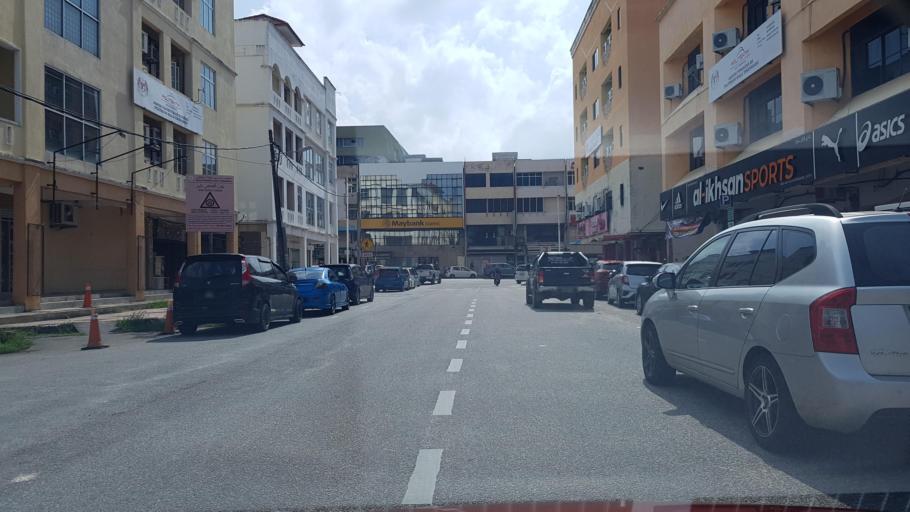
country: MY
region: Terengganu
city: Kuala Terengganu
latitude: 5.3286
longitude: 103.1361
